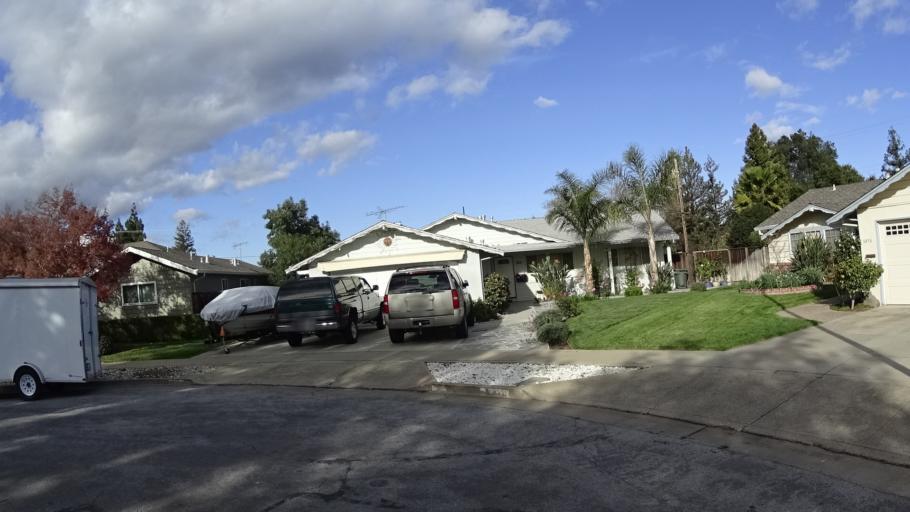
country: US
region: California
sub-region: Santa Clara County
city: Sunnyvale
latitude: 37.3496
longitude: -122.0589
